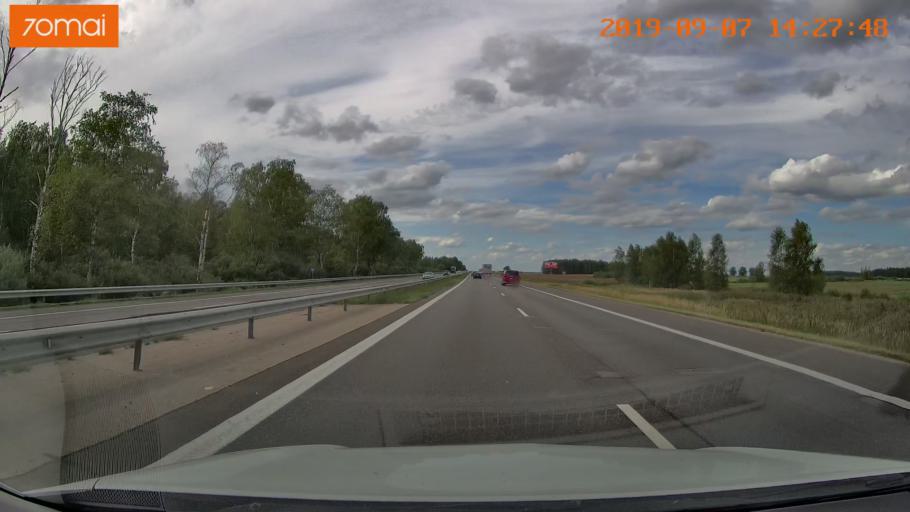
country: LT
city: Kaisiadorys
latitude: 54.8496
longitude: 24.3149
